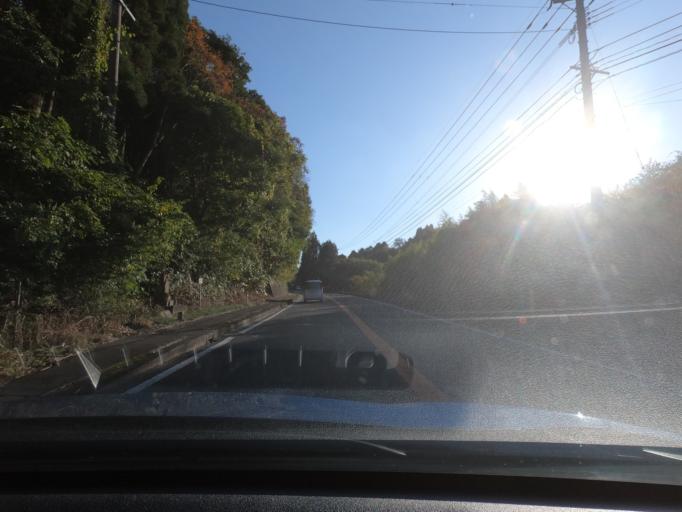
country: JP
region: Kagoshima
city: Akune
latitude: 32.0521
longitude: 130.2211
